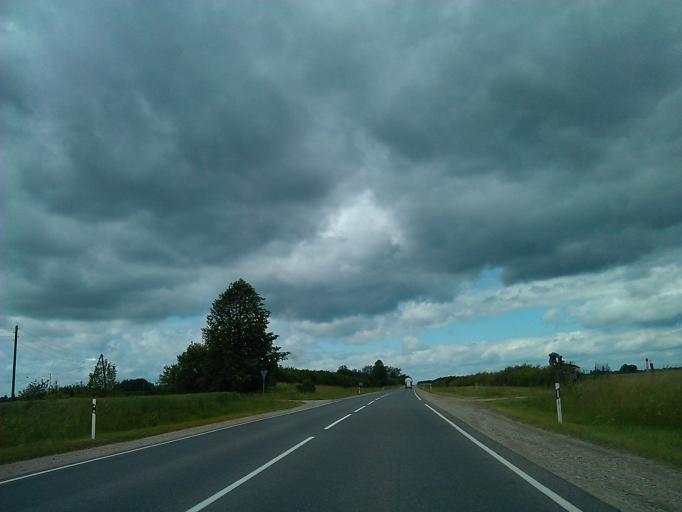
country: LV
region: Engure
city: Smarde
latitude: 56.9203
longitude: 23.2585
